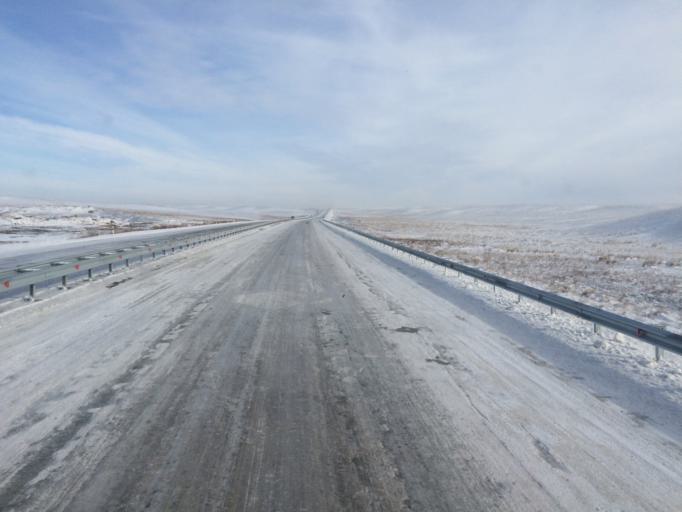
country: KZ
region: Zhambyl
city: Georgiyevka
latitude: 43.3550
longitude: 74.5706
